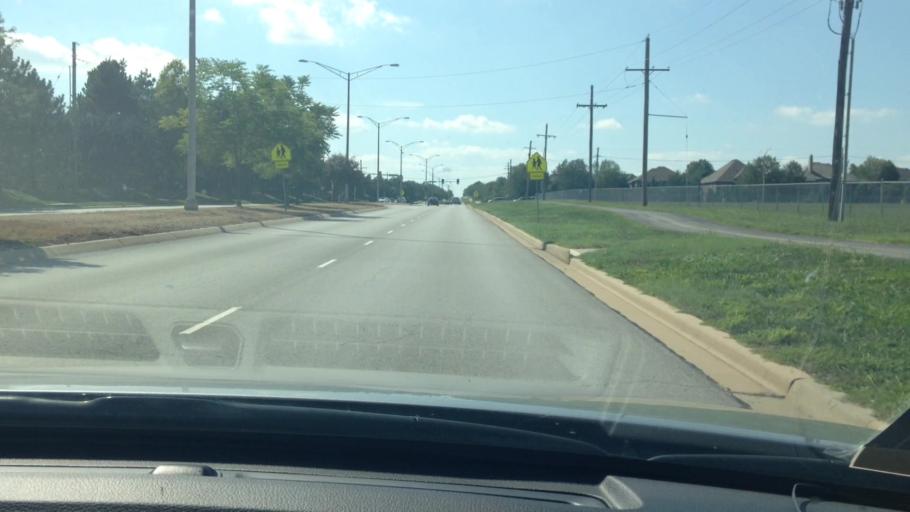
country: US
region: Kansas
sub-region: Johnson County
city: Lenexa
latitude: 38.8692
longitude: -94.6979
